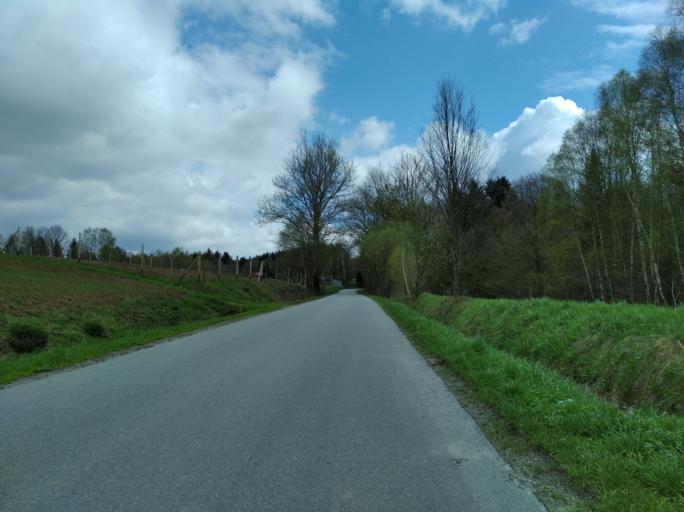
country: PL
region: Subcarpathian Voivodeship
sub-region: Powiat strzyzowski
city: Polomia
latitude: 49.8869
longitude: 21.9152
